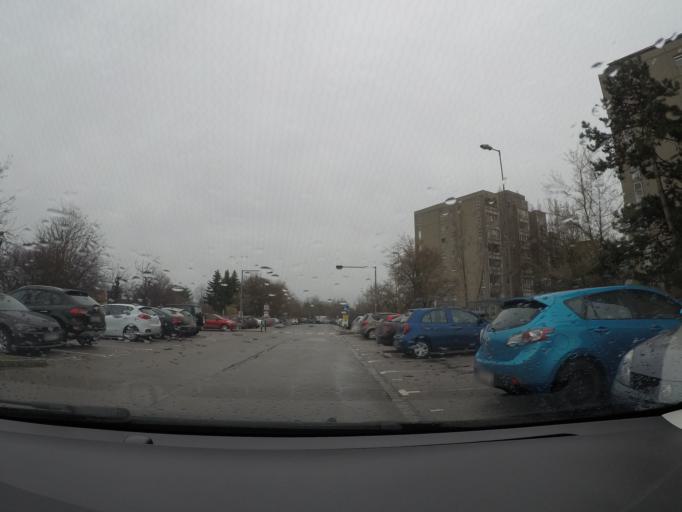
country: AT
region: Lower Austria
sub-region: Politischer Bezirk Modling
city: Wiener Neudorf
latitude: 48.0911
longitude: 16.3110
